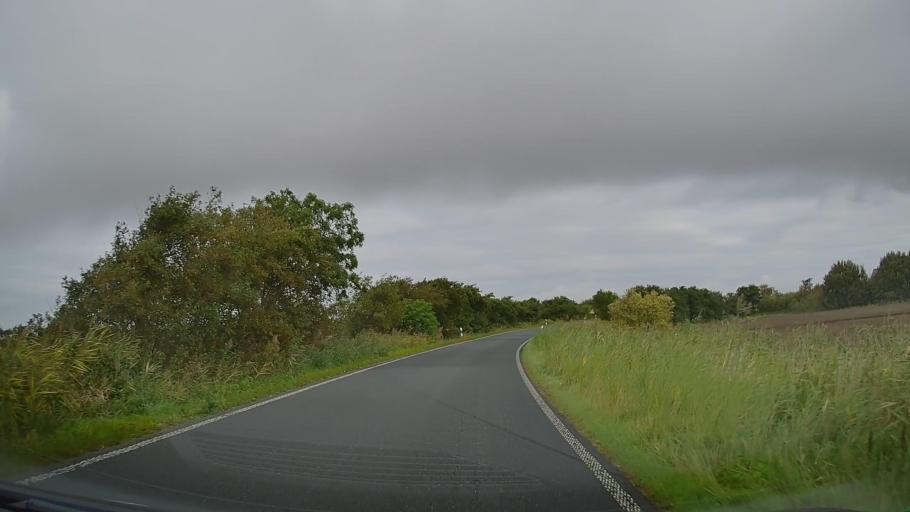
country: DE
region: Schleswig-Holstein
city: Galmsbull
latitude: 54.7700
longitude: 8.7158
